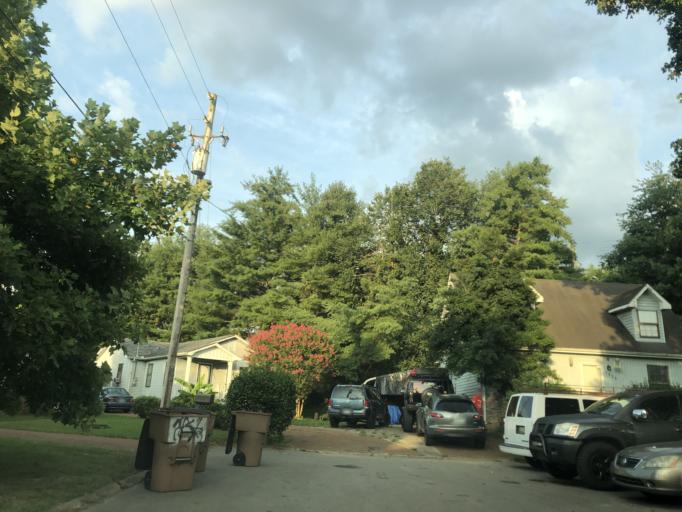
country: US
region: Tennessee
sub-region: Davidson County
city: Nashville
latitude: 36.1625
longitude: -86.7013
